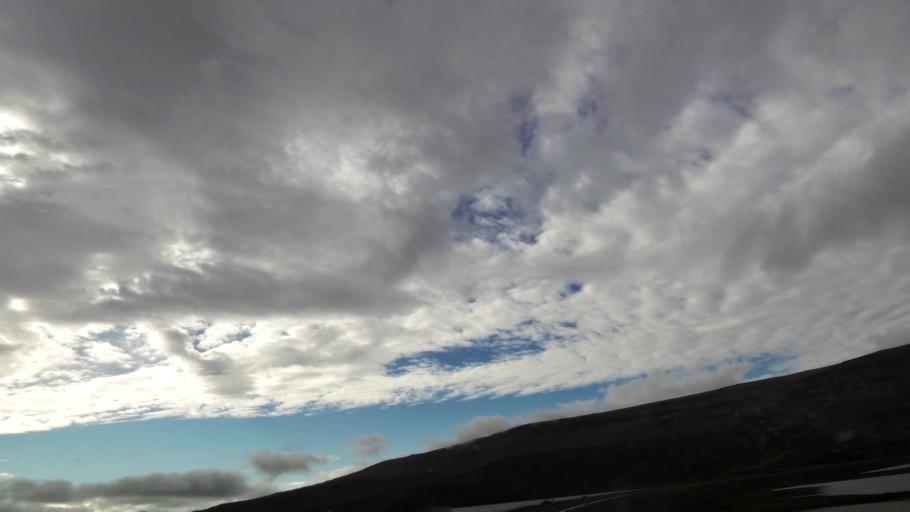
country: IS
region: West
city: Olafsvik
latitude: 65.5316
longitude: -23.7849
